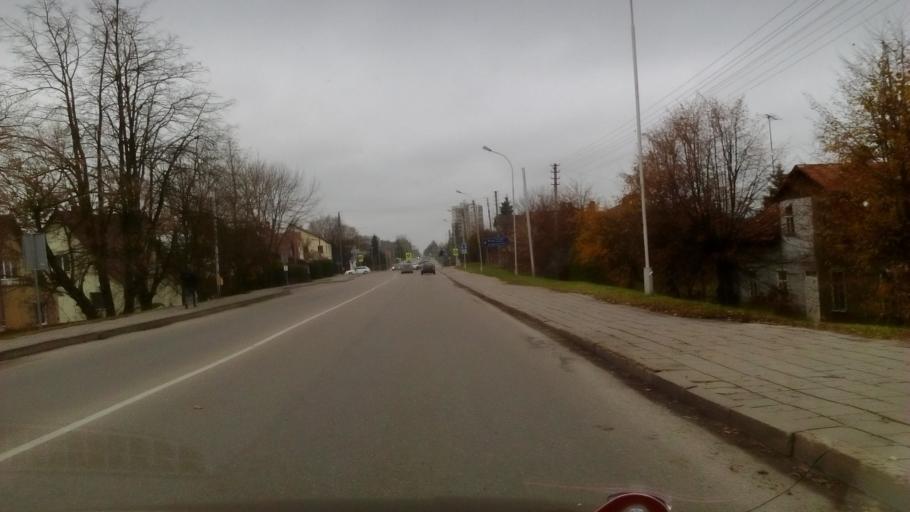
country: LT
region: Marijampoles apskritis
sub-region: Marijampole Municipality
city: Marijampole
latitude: 54.5595
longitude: 23.3445
